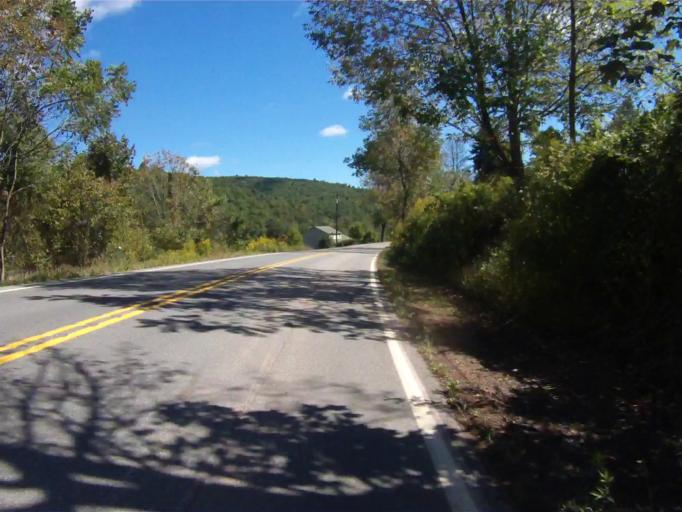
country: US
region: Pennsylvania
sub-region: Centre County
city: Park Forest Village
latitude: 40.9316
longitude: -77.9127
